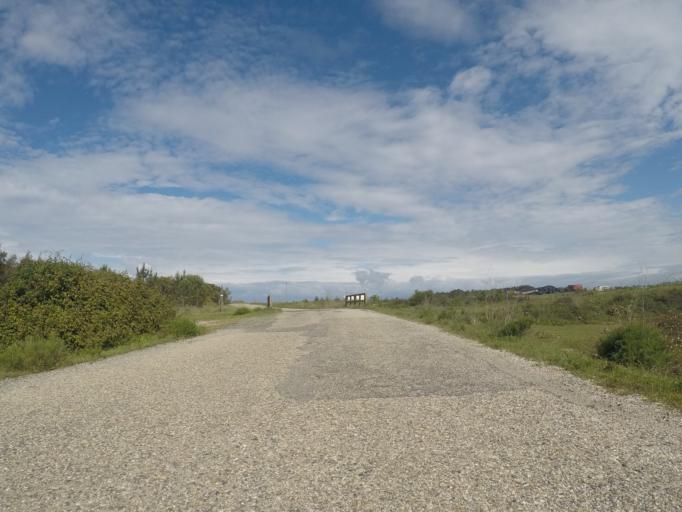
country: PT
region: Beja
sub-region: Odemira
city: Sao Teotonio
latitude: 37.4491
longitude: -8.7653
